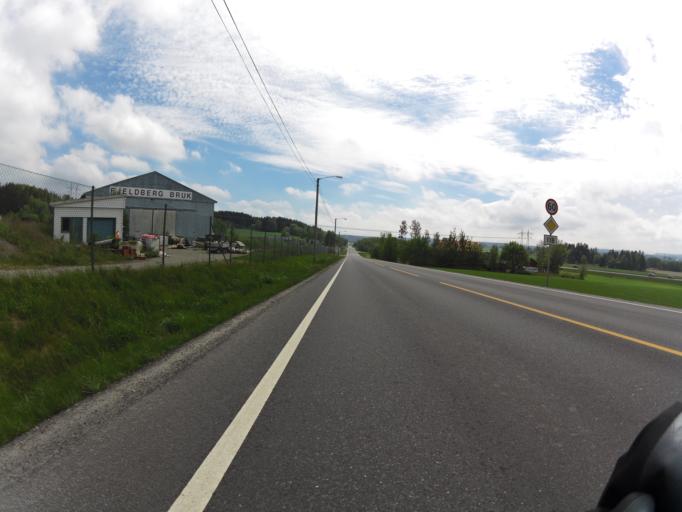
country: NO
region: Ostfold
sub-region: Rade
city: Karlshus
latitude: 59.3426
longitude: 10.9327
